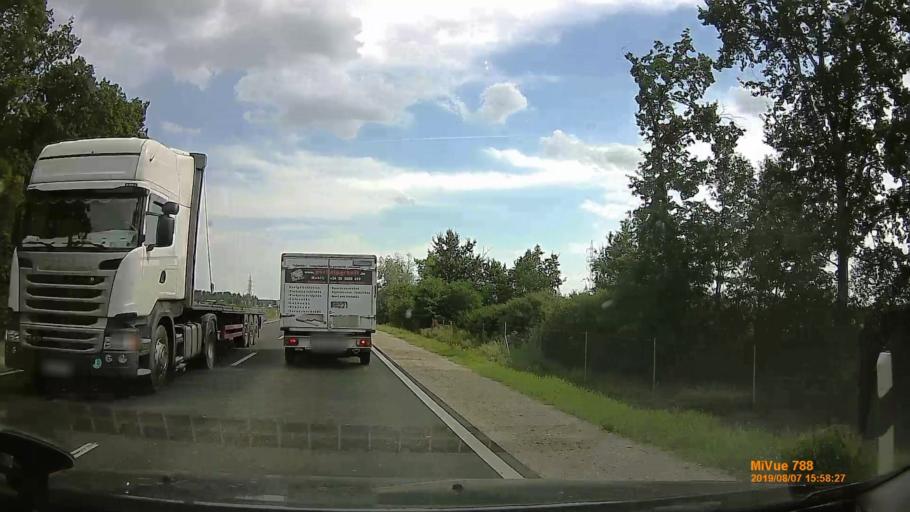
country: HU
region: Vas
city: Kormend
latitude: 47.0266
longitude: 16.6131
